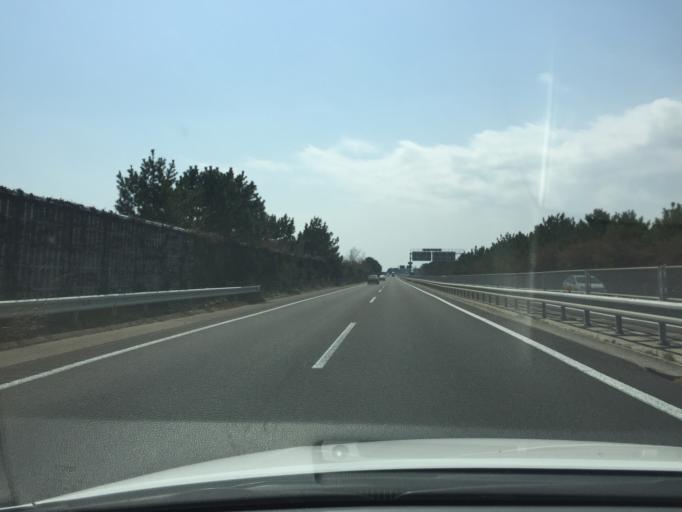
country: JP
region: Miyagi
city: Sendai
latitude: 38.2020
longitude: 140.9432
